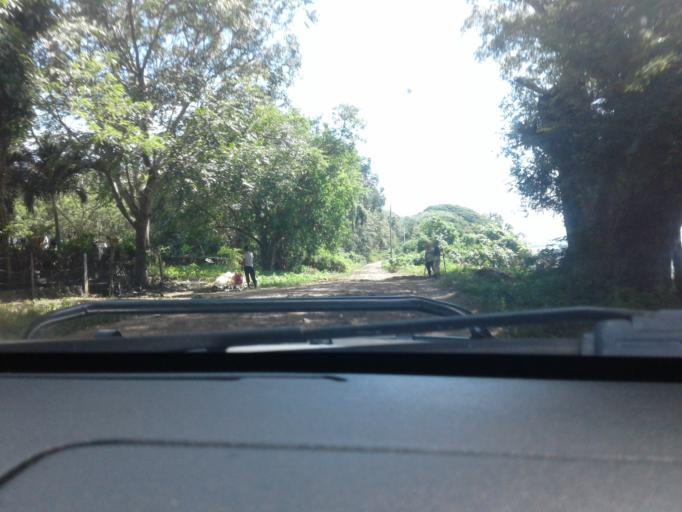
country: NI
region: Rivas
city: Altagracia
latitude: 11.4215
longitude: -85.5464
